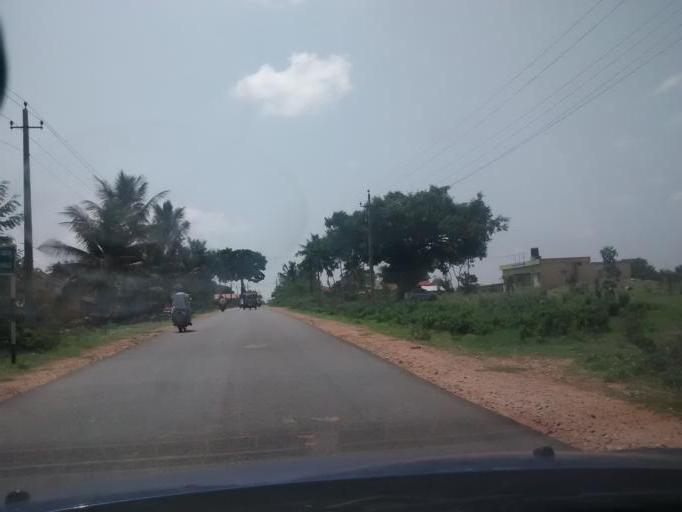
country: IN
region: Karnataka
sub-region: Hassan
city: Konanur
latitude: 12.5811
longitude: 76.2024
